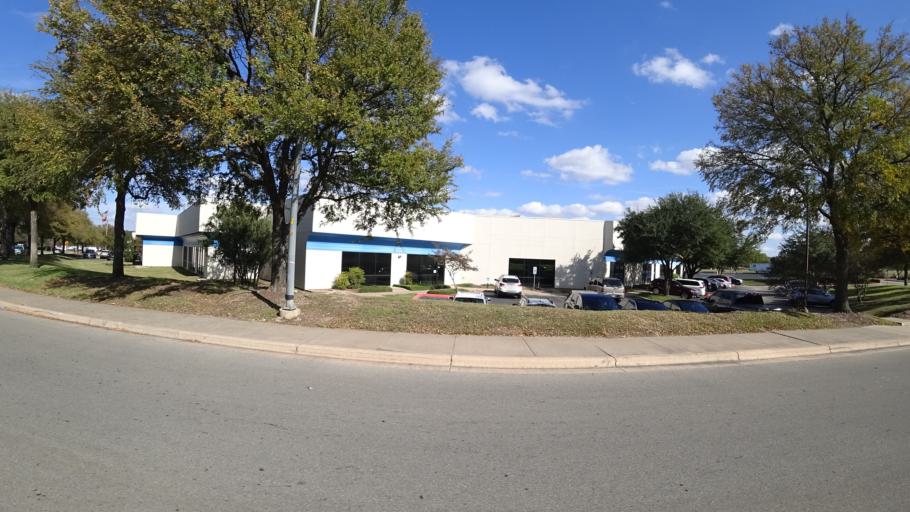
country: US
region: Texas
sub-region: Travis County
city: Wells Branch
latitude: 30.4738
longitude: -97.6782
